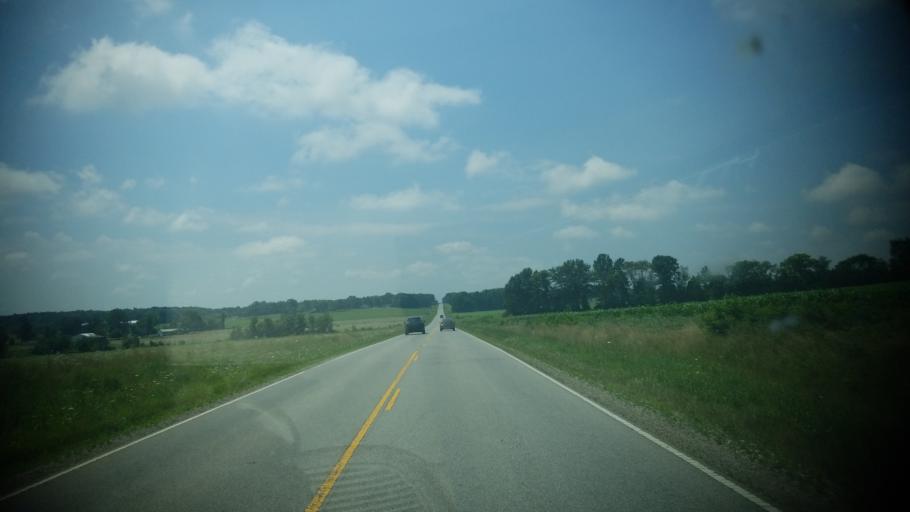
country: US
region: Illinois
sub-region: Wayne County
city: Fairfield
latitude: 38.4249
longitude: -88.3498
